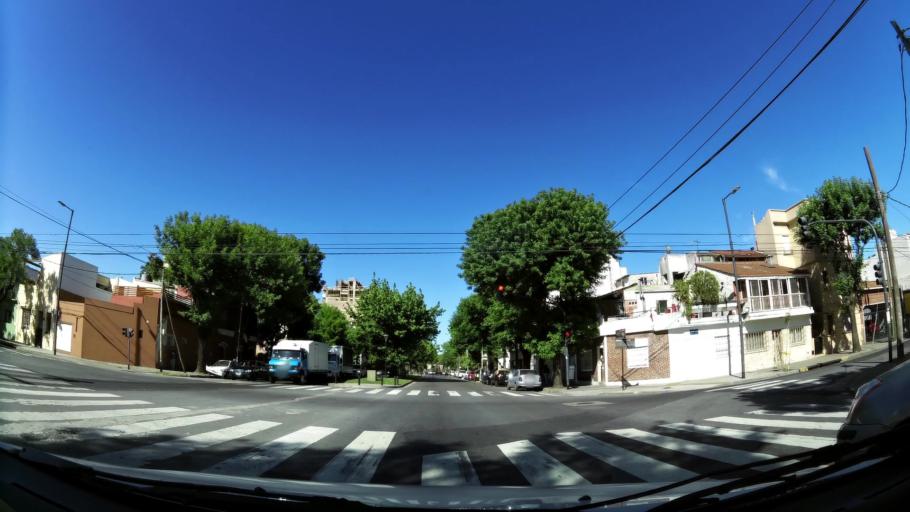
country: AR
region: Buenos Aires
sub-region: Partido de General San Martin
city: General San Martin
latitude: -34.5537
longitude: -58.4920
